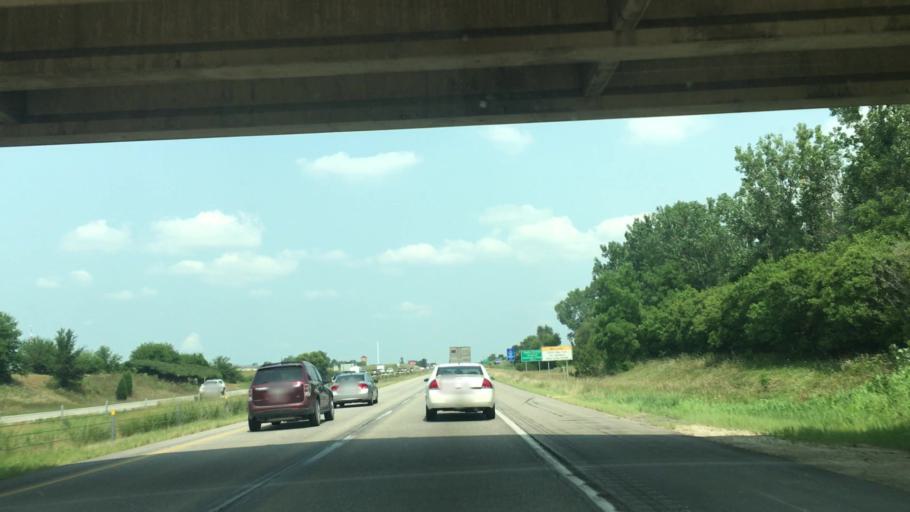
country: US
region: Iowa
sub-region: Linn County
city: Ely
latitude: 41.8762
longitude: -91.6701
